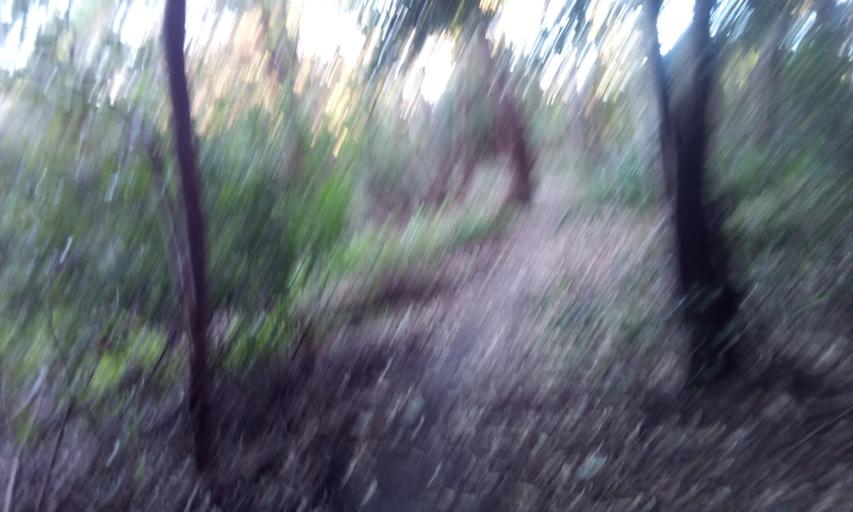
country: AU
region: New South Wales
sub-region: Wollongong
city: Keiraville
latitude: -34.4090
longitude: 150.8616
